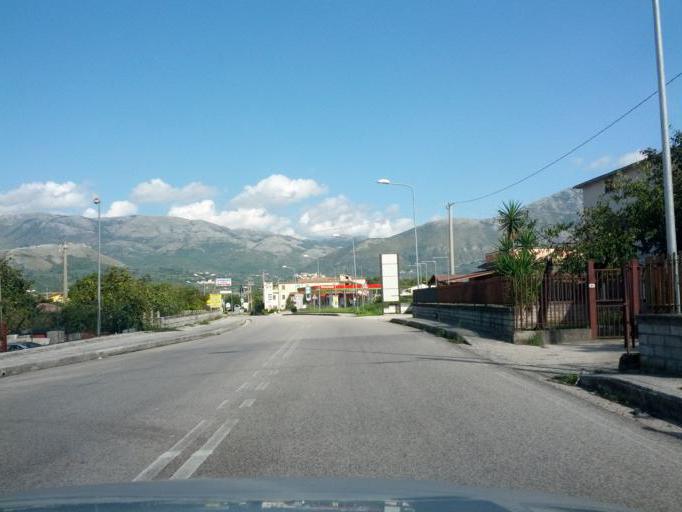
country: IT
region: Campania
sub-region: Provincia di Caserta
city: Bivio Mortola
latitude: 41.4342
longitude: 13.9045
